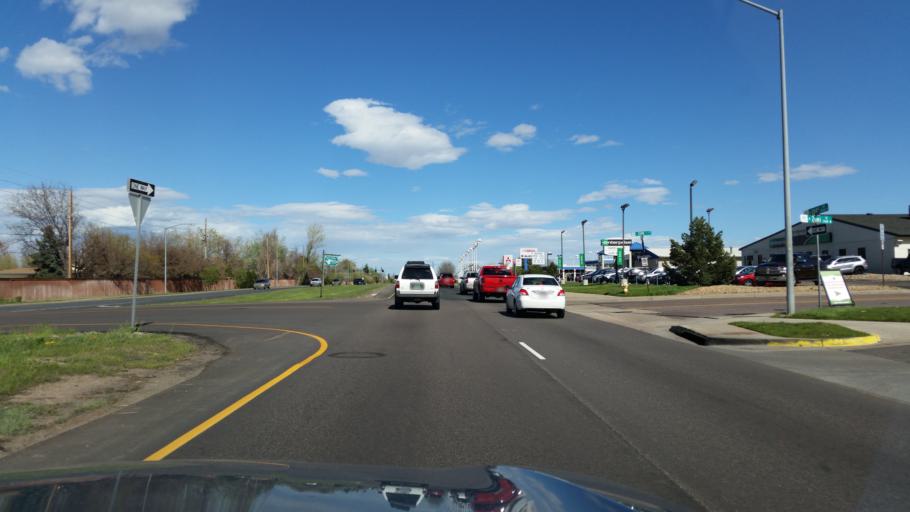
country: US
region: Colorado
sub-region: Adams County
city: Northglenn
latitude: 39.8850
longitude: -105.0160
